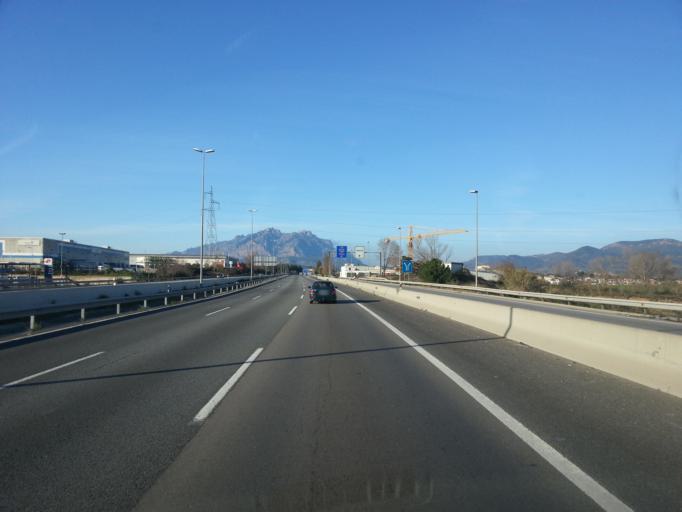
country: ES
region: Catalonia
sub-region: Provincia de Barcelona
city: Abrera
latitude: 41.5068
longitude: 1.9048
